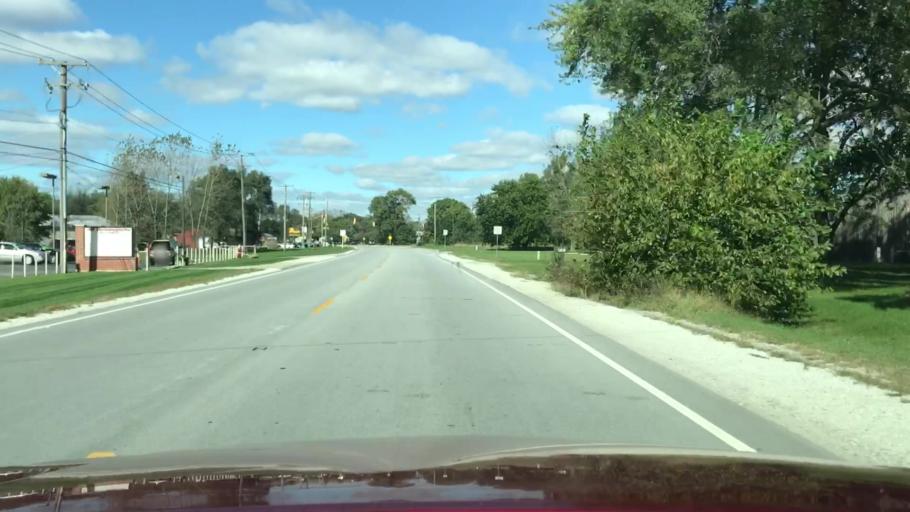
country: US
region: Illinois
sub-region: Cook County
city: Lynwood
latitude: 41.5126
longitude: -87.5372
